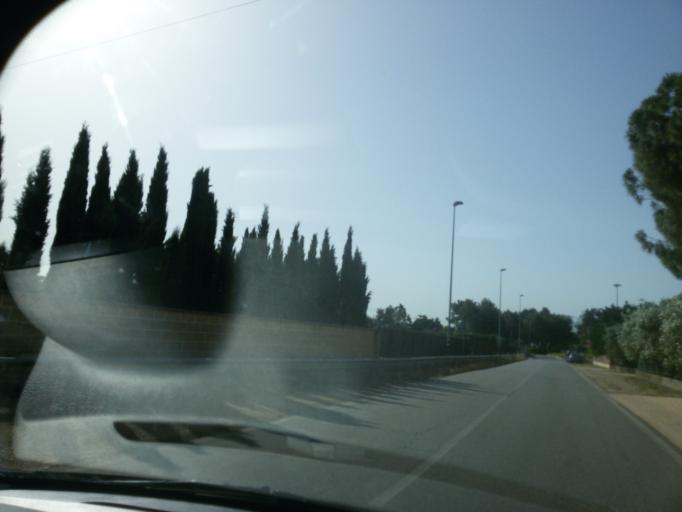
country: IT
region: Apulia
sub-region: Provincia di Brindisi
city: Mesagne
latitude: 40.5434
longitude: 17.8155
